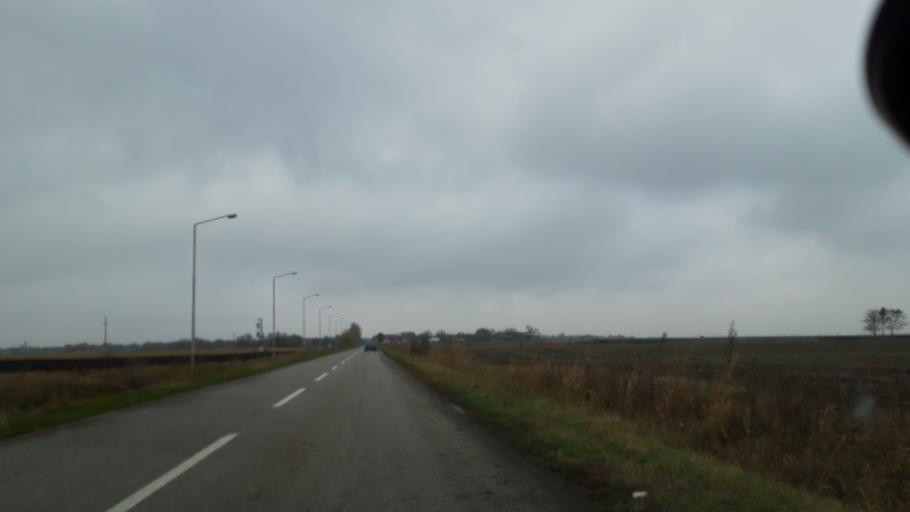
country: RS
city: Backo Gradiste
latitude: 45.5009
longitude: 19.9430
